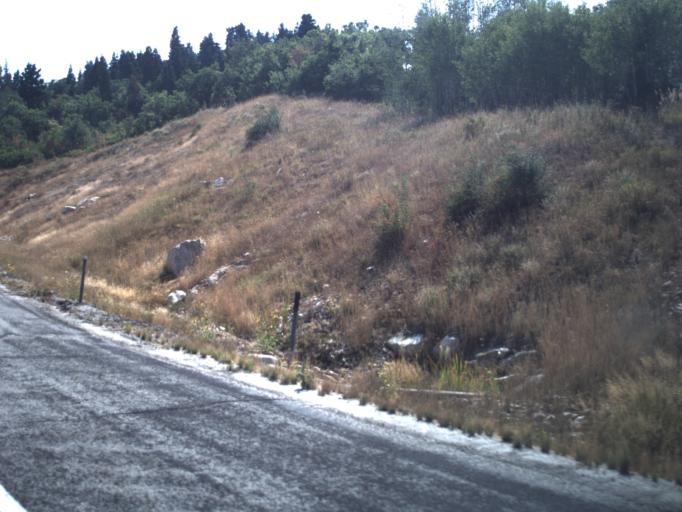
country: US
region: Utah
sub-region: Morgan County
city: Mountain Green
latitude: 41.2058
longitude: -111.8349
